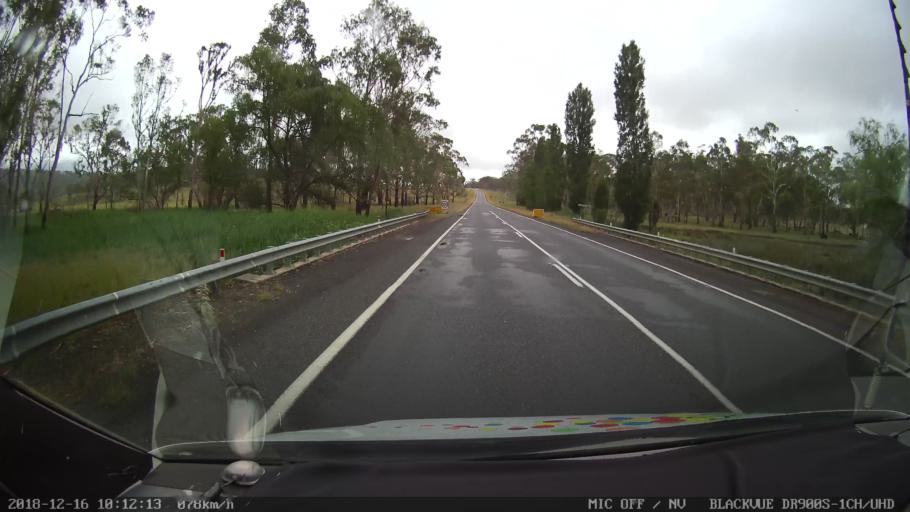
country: AU
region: New South Wales
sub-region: Glen Innes Severn
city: Glen Innes
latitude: -29.3073
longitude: 151.9383
